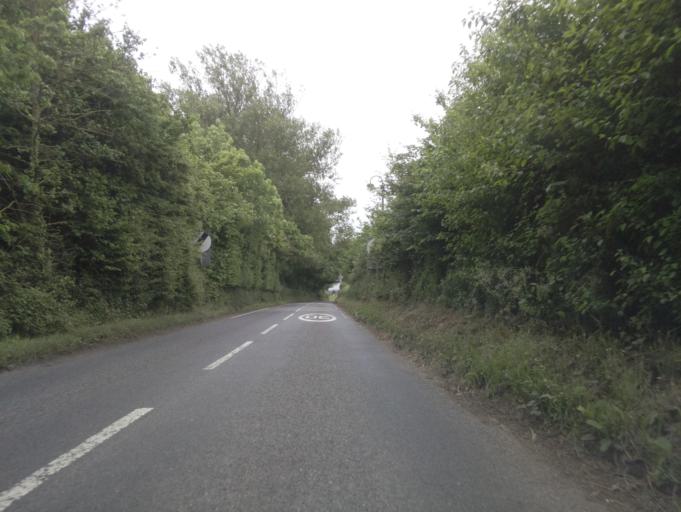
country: GB
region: England
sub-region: Somerset
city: Yeovil
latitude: 51.0174
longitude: -2.5782
